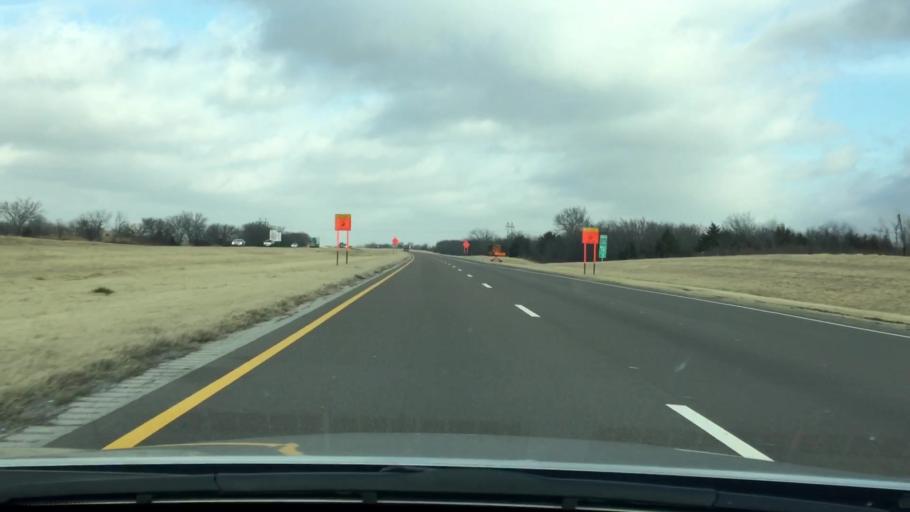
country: US
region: Oklahoma
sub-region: Garvin County
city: Maysville
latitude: 34.8303
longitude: -97.3105
